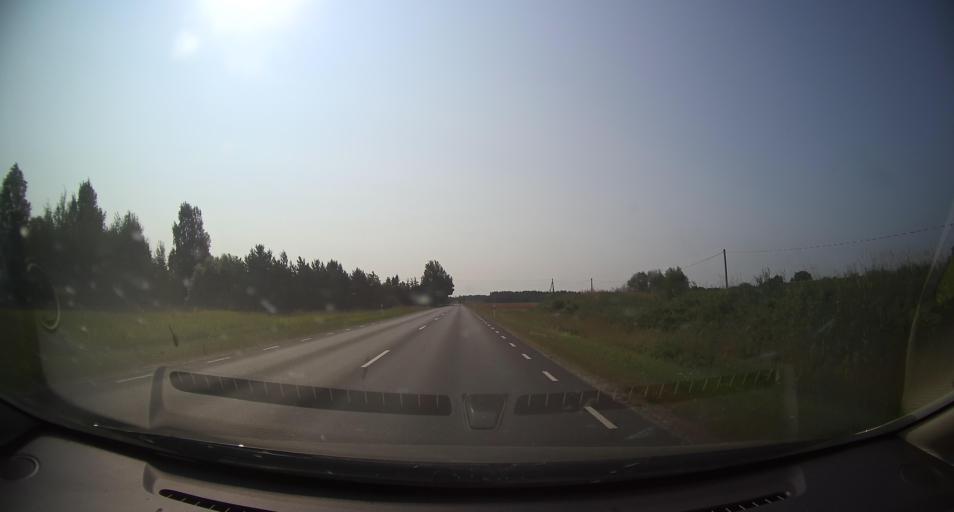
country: EE
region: Paernumaa
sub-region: Audru vald
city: Audru
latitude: 58.4521
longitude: 24.2235
